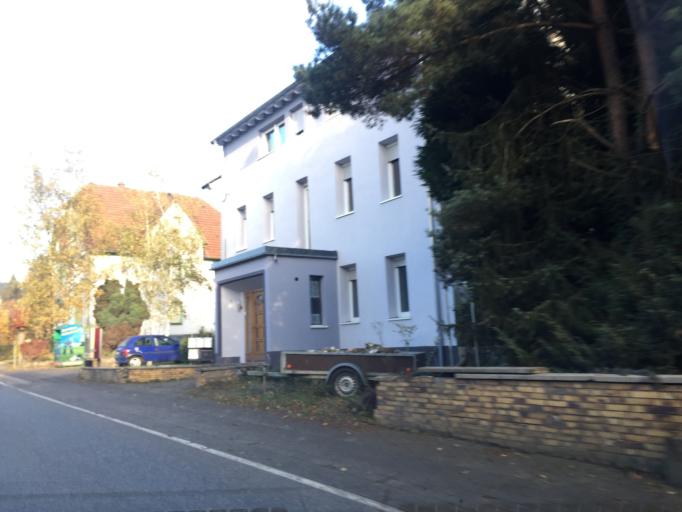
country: DE
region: Rheinland-Pfalz
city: Dreikirchen
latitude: 50.4473
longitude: 7.9423
